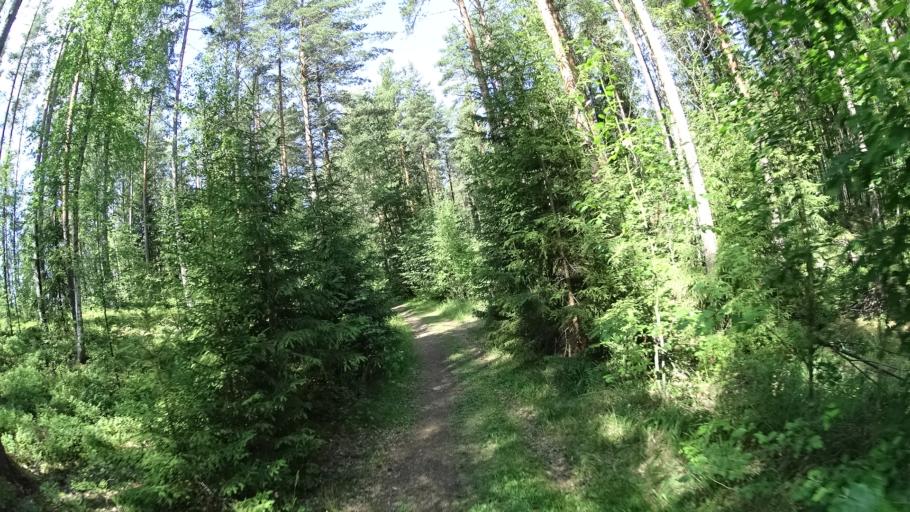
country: FI
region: Haeme
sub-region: Forssa
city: Tammela
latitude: 60.7706
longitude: 23.8680
